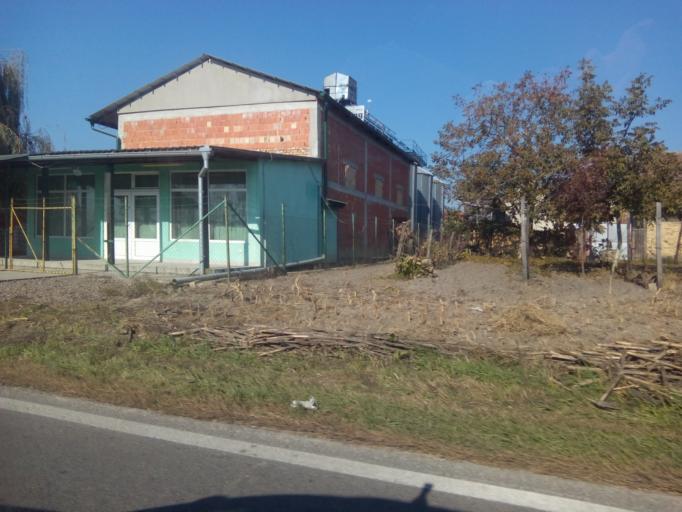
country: RS
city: Glozan
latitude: 45.2751
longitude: 19.5650
